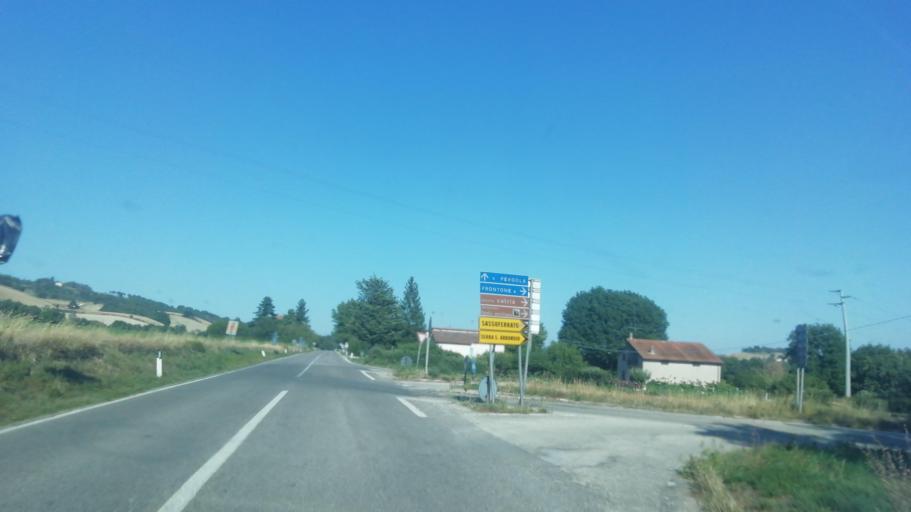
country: IT
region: The Marches
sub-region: Provincia di Pesaro e Urbino
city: Frontone
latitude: 43.5437
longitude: 12.7705
